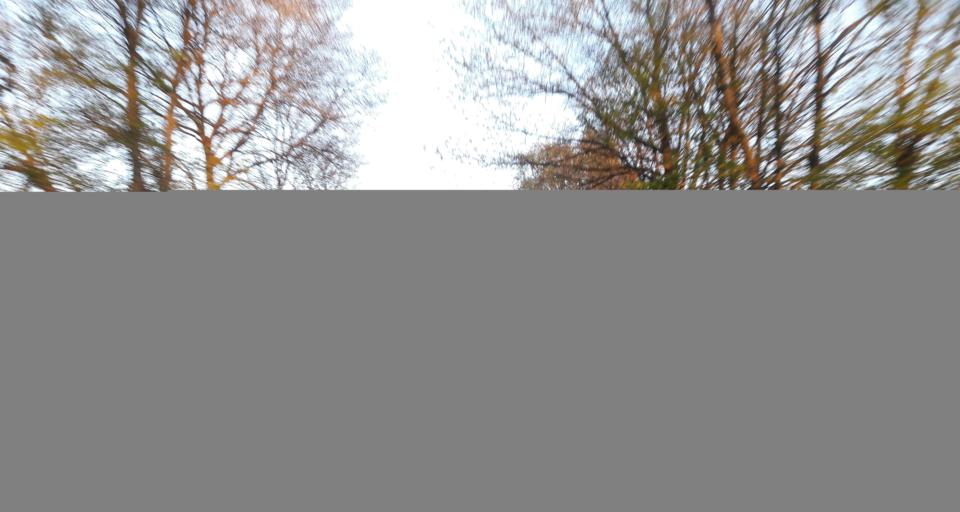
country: DE
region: Rheinland-Pfalz
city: Longkamp
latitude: 49.8794
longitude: 7.1028
